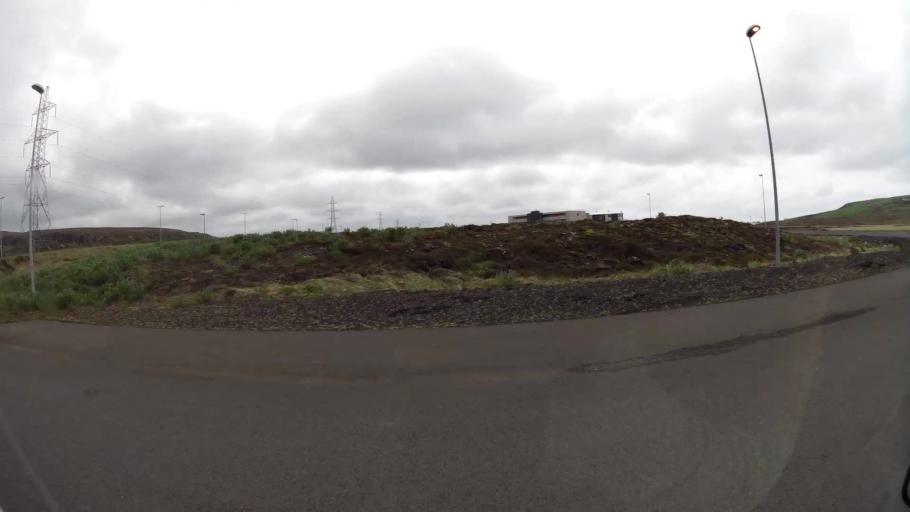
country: IS
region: Capital Region
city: Hafnarfjoerdur
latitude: 64.0442
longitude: -21.9559
